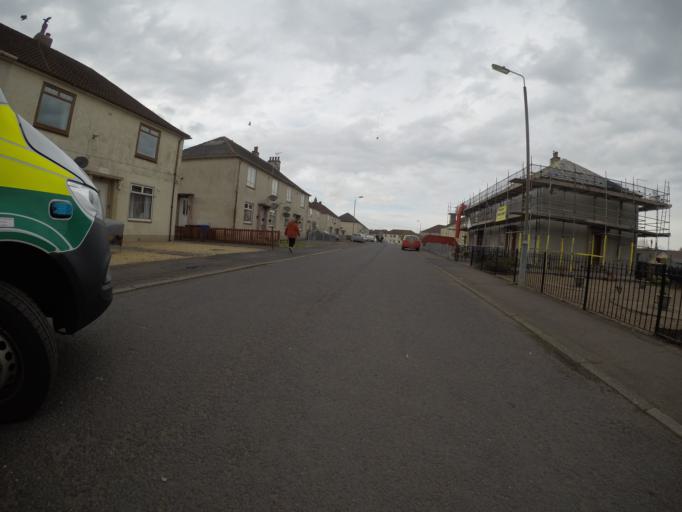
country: GB
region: Scotland
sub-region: East Ayrshire
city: Kilmaurs
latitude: 55.6399
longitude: -4.5293
